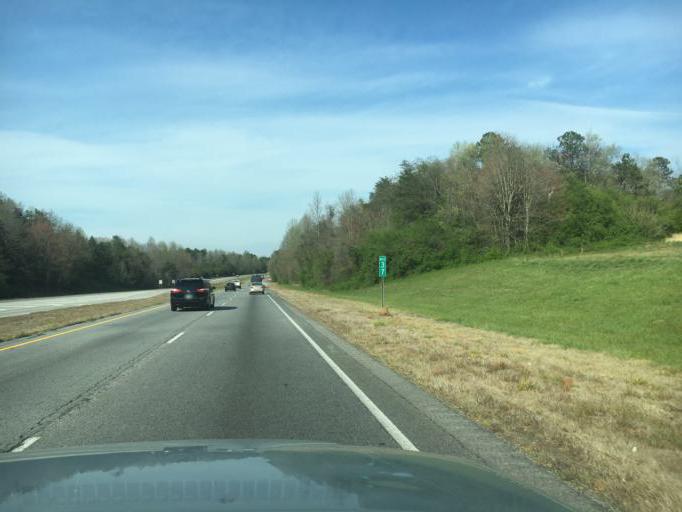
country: US
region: Georgia
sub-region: Habersham County
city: Raoul
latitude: 34.4401
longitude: -83.6279
